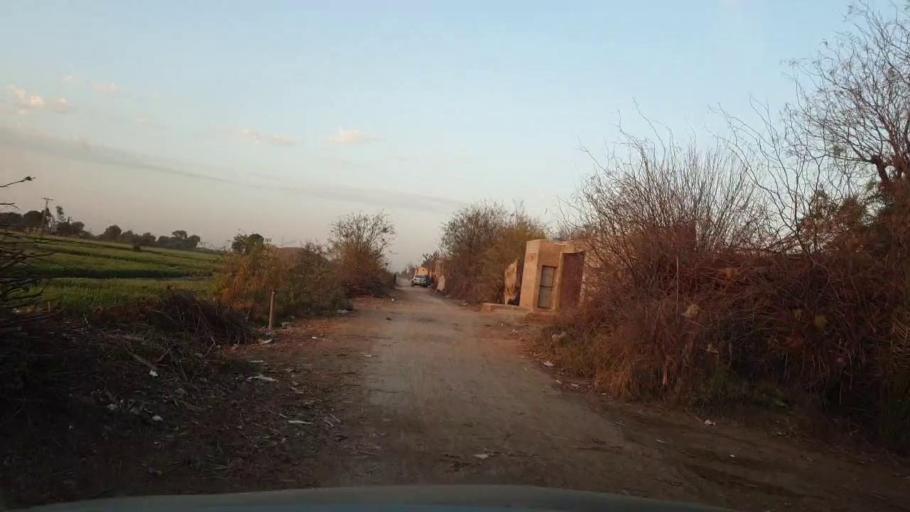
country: PK
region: Sindh
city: Matiari
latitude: 25.6007
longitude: 68.4798
